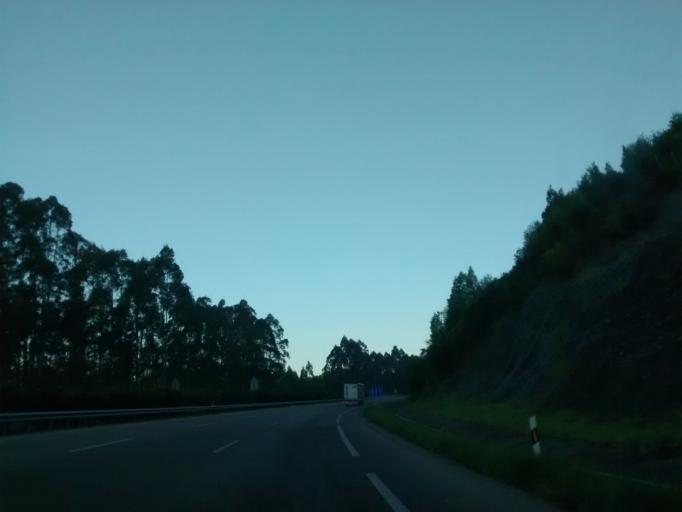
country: ES
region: Asturias
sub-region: Province of Asturias
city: Colunga
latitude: 43.4957
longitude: -5.3273
